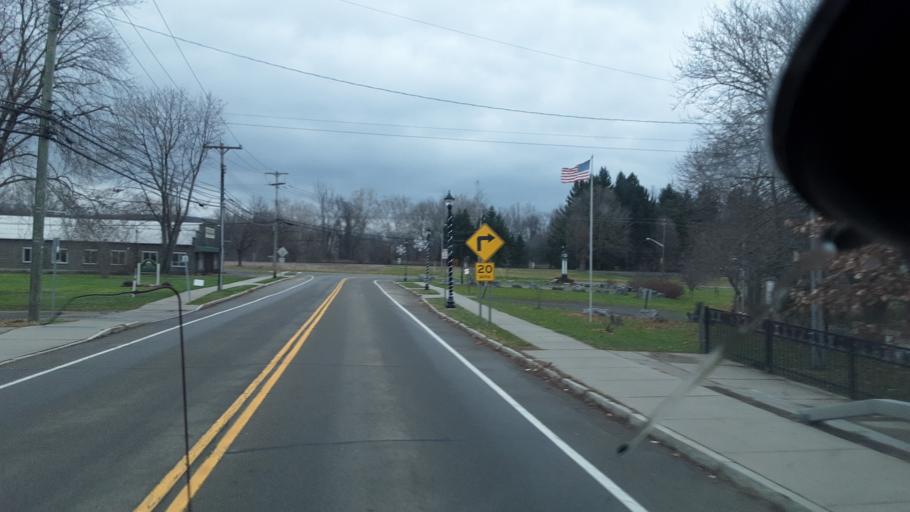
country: US
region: New York
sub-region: Allegany County
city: Belmont
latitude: 42.2243
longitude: -78.0305
